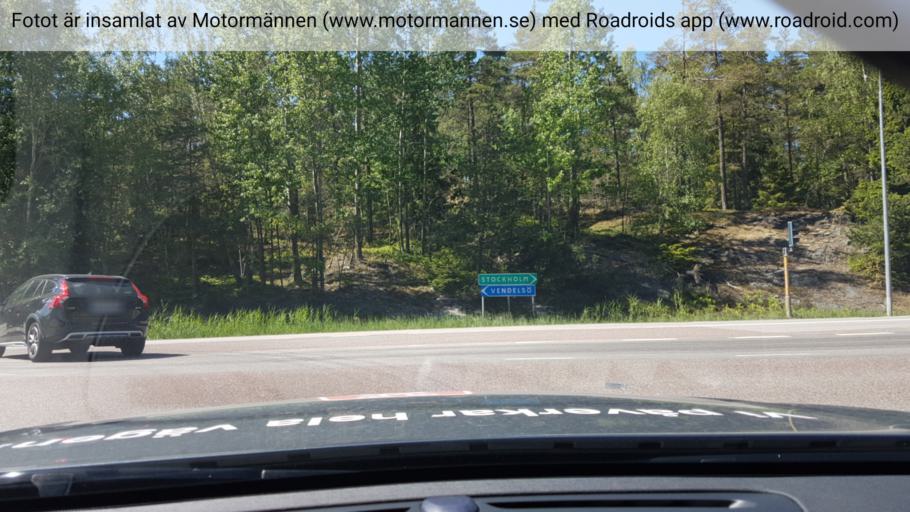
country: SE
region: Stockholm
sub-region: Nacka Kommun
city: Alta
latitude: 59.2337
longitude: 18.1934
